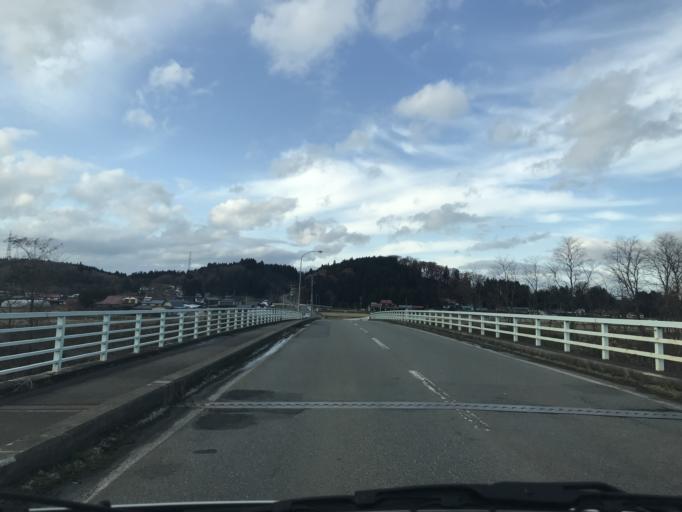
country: JP
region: Iwate
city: Mizusawa
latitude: 39.1663
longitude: 141.0899
